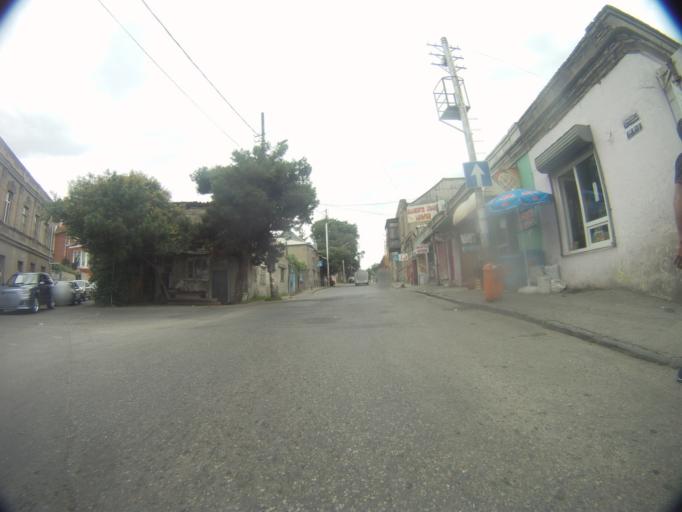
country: GE
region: T'bilisi
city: Tbilisi
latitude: 41.6838
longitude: 44.8765
